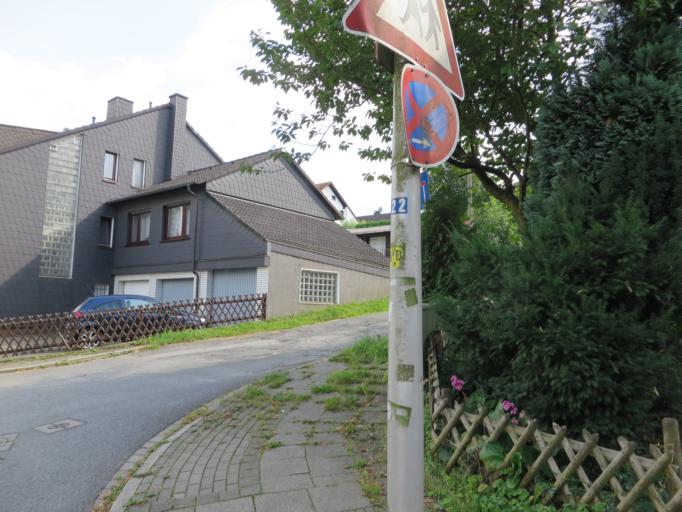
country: DE
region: North Rhine-Westphalia
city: Witten
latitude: 51.4486
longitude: 7.4037
